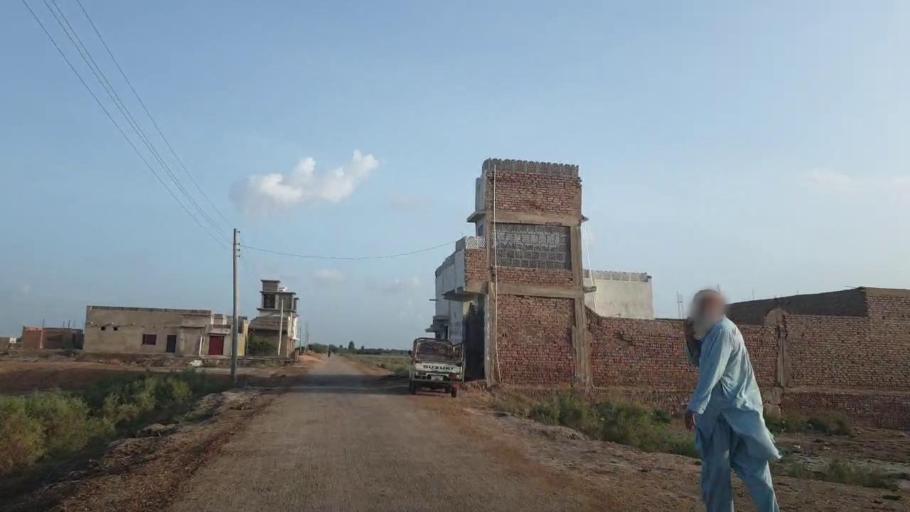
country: PK
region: Sindh
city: Kadhan
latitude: 24.6388
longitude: 69.1228
